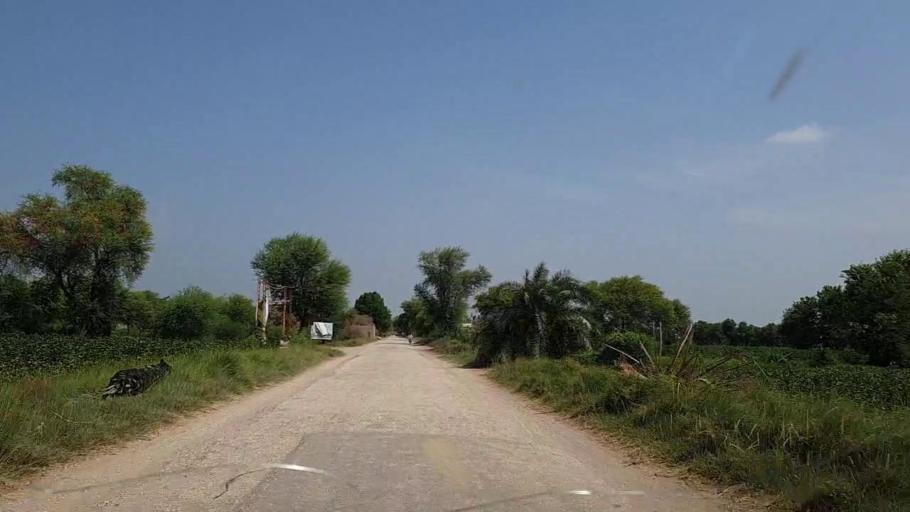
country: PK
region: Sindh
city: Adilpur
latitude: 27.8286
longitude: 69.2950
